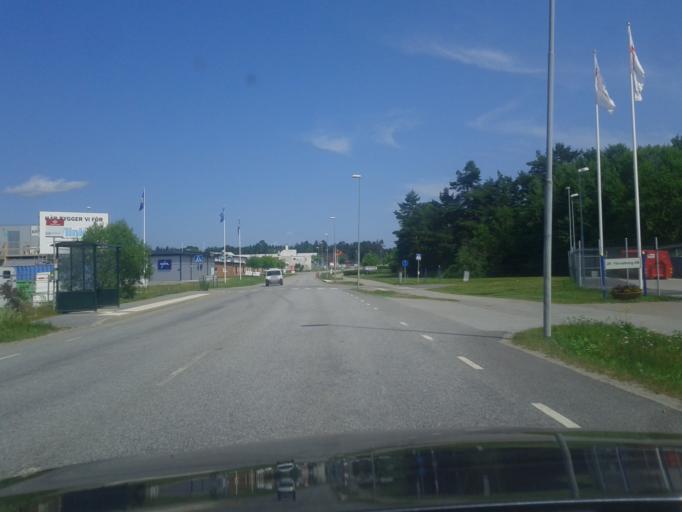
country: SE
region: Stockholm
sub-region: Taby Kommun
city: Taby
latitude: 59.4663
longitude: 18.1267
